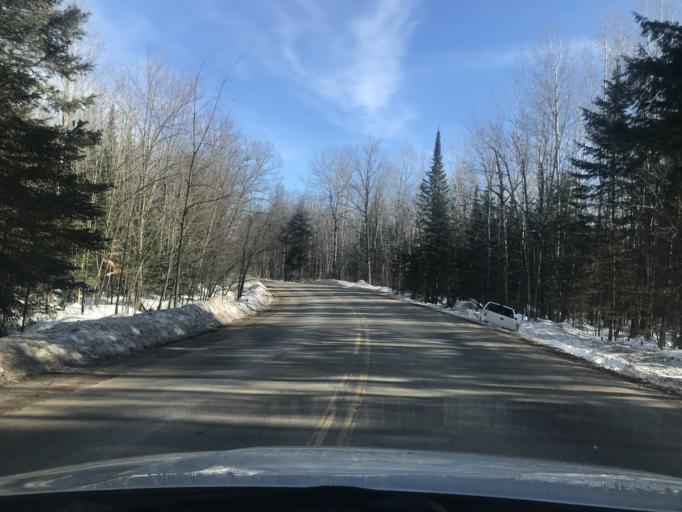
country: US
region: Michigan
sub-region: Dickinson County
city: Kingsford
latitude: 45.4039
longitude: -88.3751
